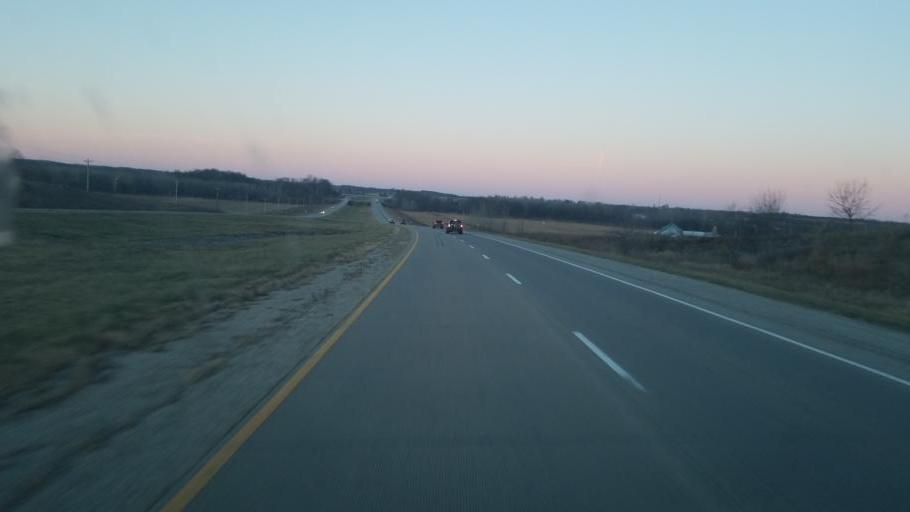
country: US
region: Iowa
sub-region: Henry County
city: Mount Pleasant
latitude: 40.9760
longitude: -91.6674
